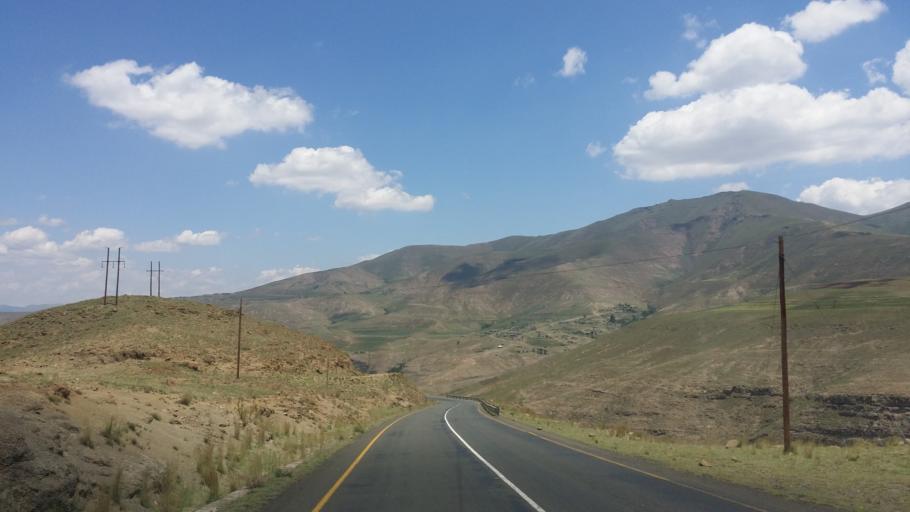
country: LS
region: Mokhotlong
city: Mokhotlong
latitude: -29.2953
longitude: 29.0051
